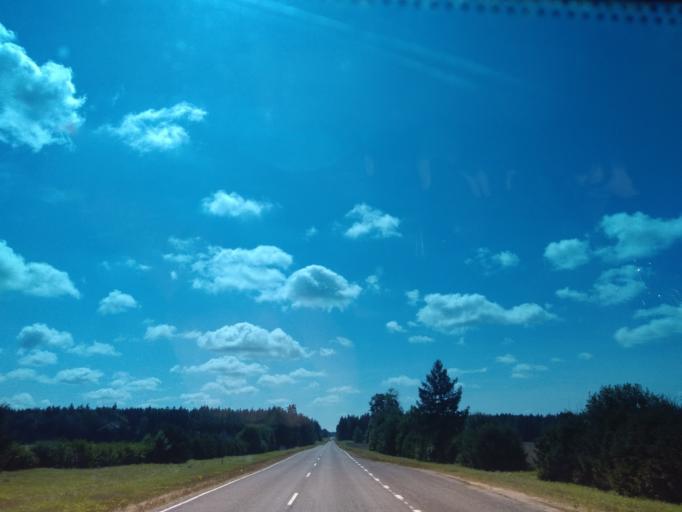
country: BY
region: Minsk
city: Uzda
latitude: 53.3359
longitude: 27.2295
